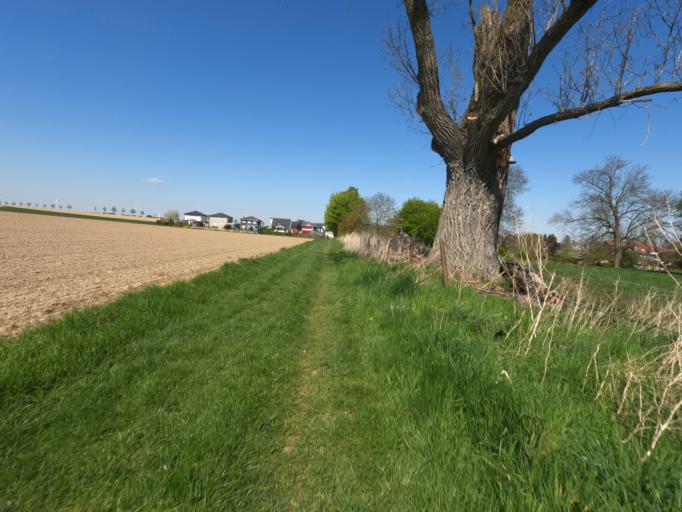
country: DE
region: North Rhine-Westphalia
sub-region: Regierungsbezirk Koln
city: Linnich
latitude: 50.9467
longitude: 6.2414
